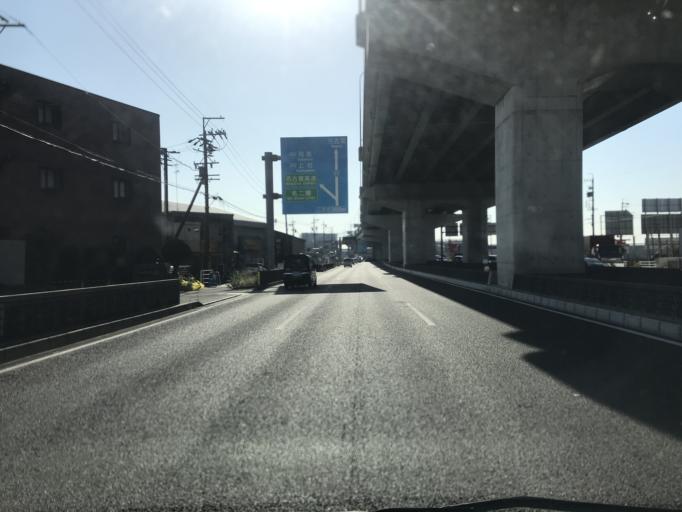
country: JP
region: Aichi
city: Iwakura
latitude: 35.2278
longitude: 136.8525
